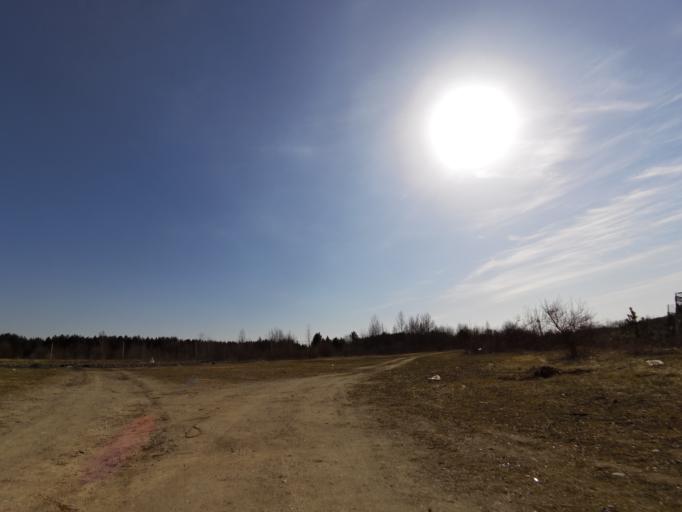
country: LT
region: Vilnius County
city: Seskine
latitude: 54.7080
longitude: 25.2600
